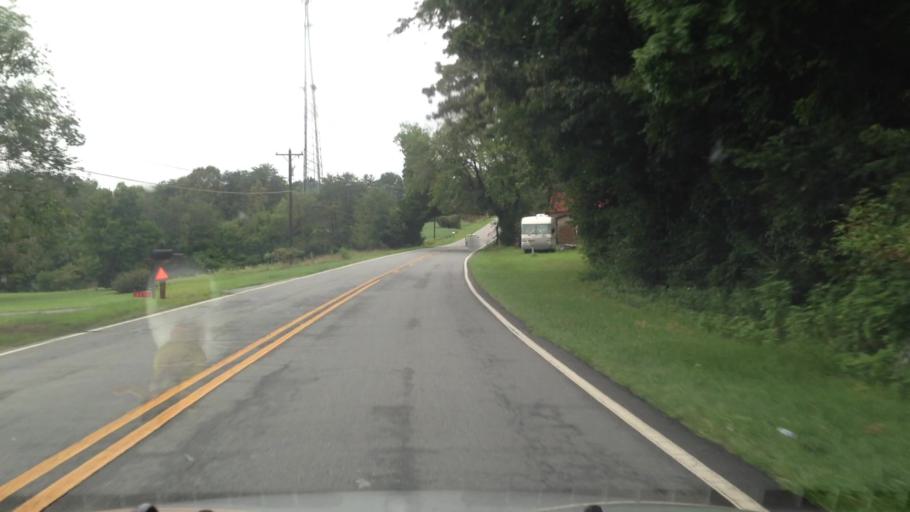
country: US
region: North Carolina
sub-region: Guilford County
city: Oak Ridge
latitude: 36.2140
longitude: -80.0564
